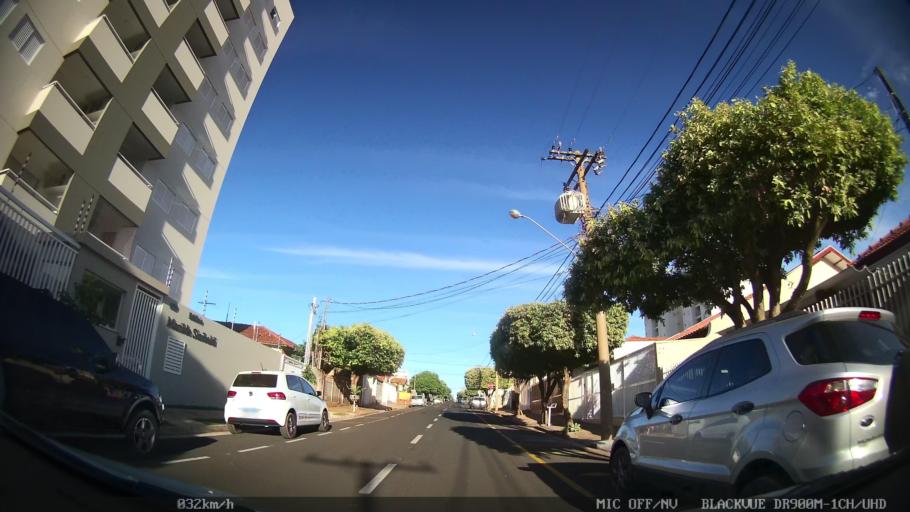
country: BR
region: Sao Paulo
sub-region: Sao Jose Do Rio Preto
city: Sao Jose do Rio Preto
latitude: -20.8258
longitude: -49.3792
